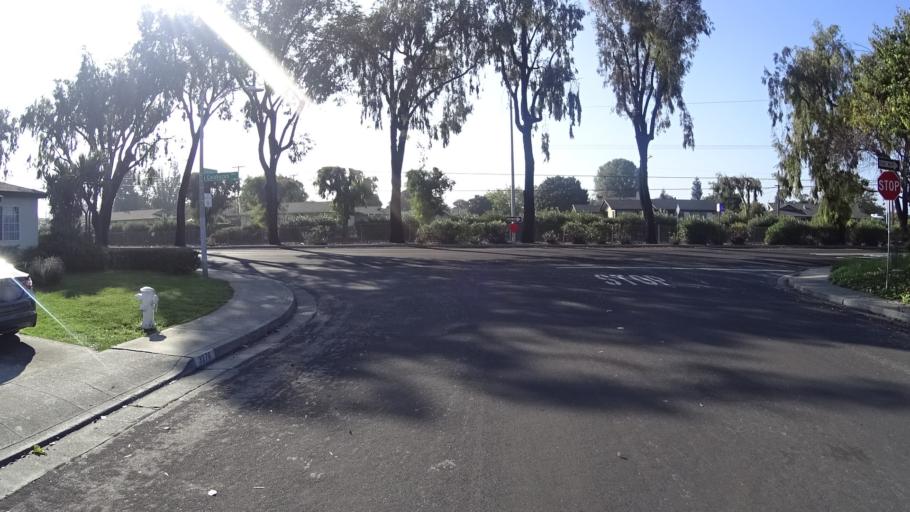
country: US
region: California
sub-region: Santa Clara County
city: Santa Clara
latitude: 37.3629
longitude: -121.9863
